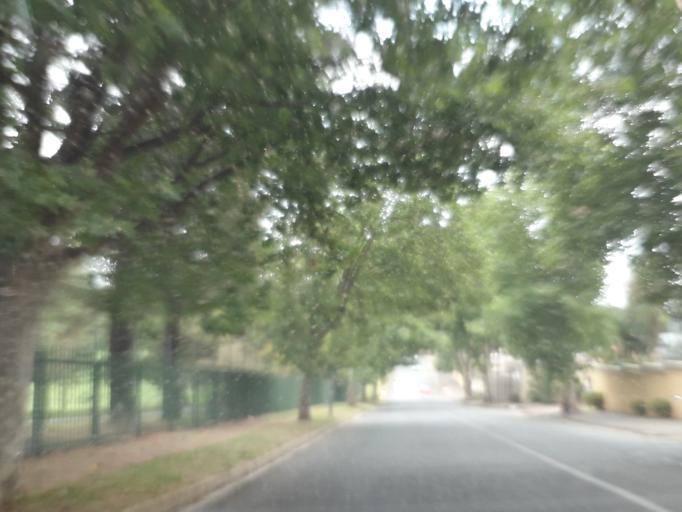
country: ZA
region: Gauteng
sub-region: City of Johannesburg Metropolitan Municipality
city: Johannesburg
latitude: -26.1609
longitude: 28.0699
